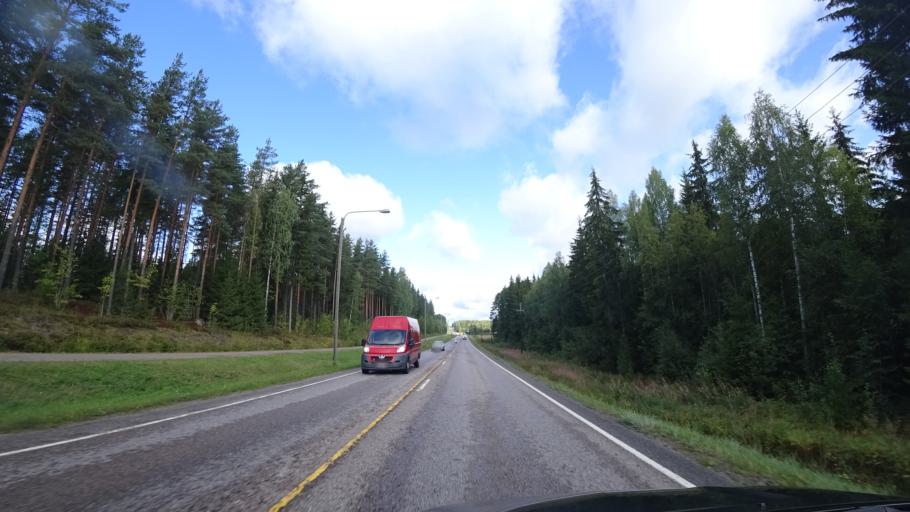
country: FI
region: Uusimaa
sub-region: Helsinki
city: Tuusula
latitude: 60.4305
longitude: 24.9924
